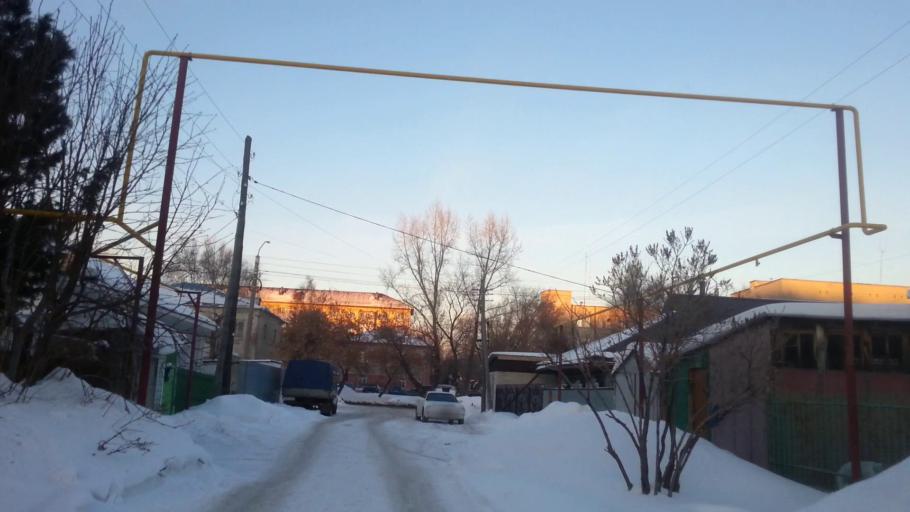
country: RU
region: Altai Krai
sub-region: Gorod Barnaulskiy
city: Barnaul
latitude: 53.3558
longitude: 83.7025
